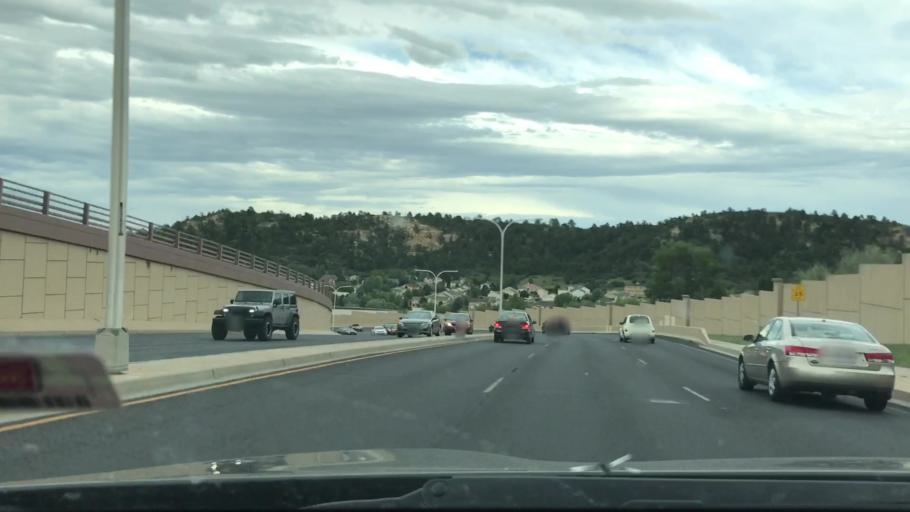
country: US
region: Colorado
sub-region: El Paso County
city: Colorado Springs
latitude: 38.8881
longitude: -104.7914
